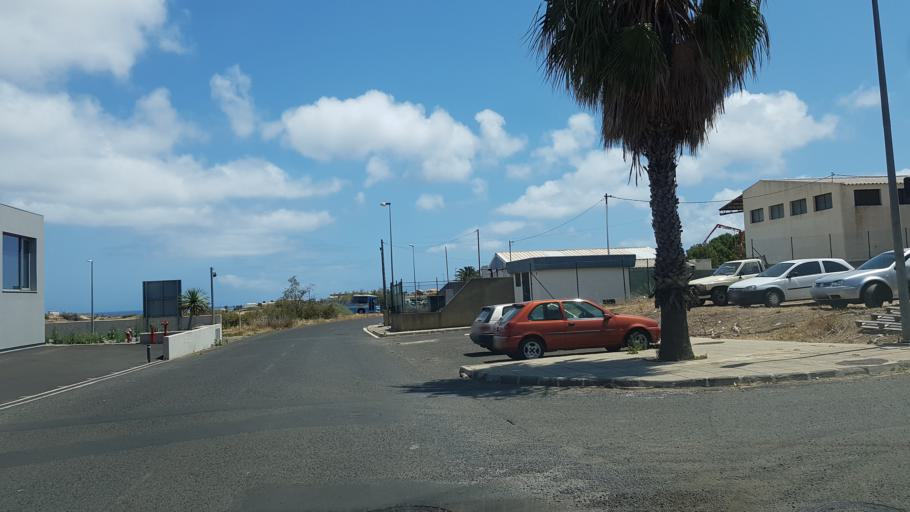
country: PT
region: Madeira
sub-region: Porto Santo
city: Camacha
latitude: 33.0720
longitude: -16.3434
